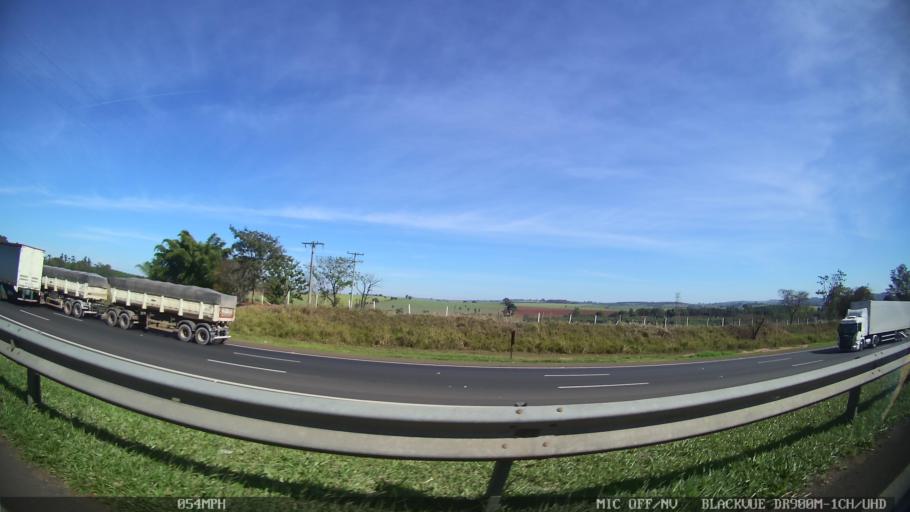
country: BR
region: Sao Paulo
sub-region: Pirassununga
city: Pirassununga
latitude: -22.0694
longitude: -47.4245
